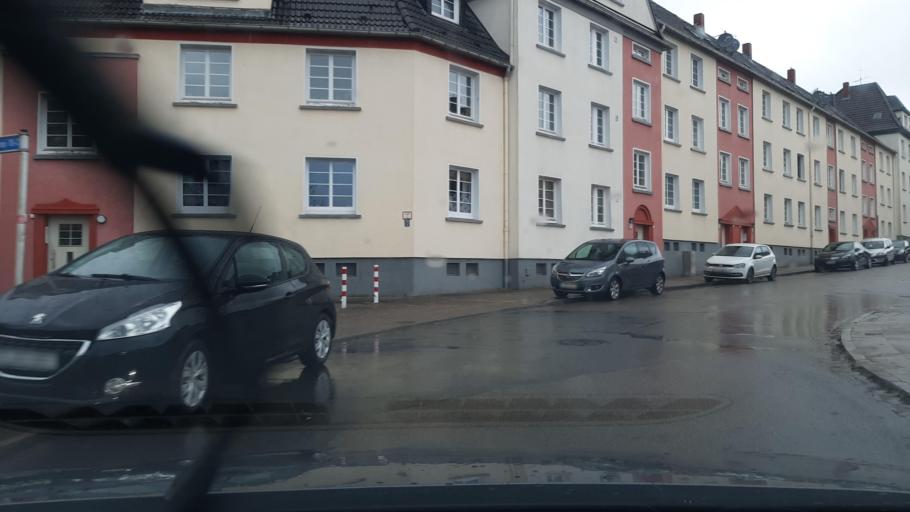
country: DE
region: North Rhine-Westphalia
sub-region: Regierungsbezirk Dusseldorf
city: Essen
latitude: 51.4399
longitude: 6.9738
